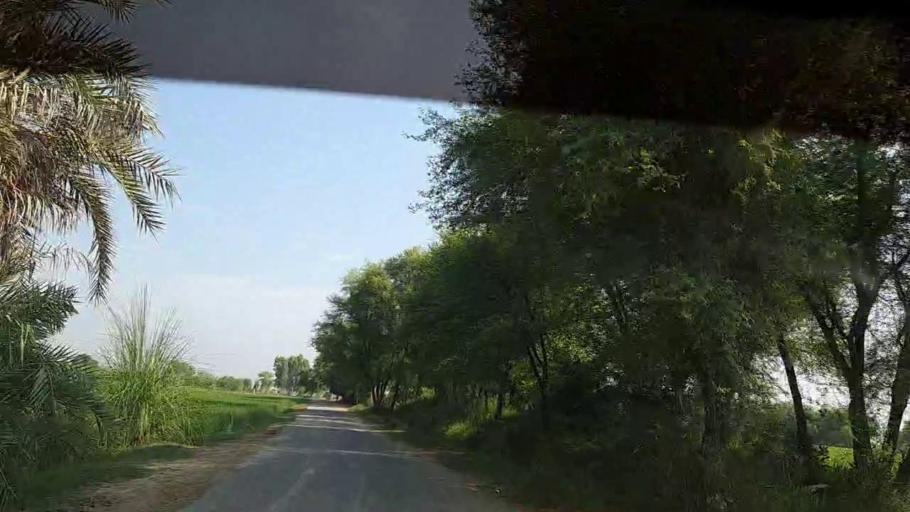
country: PK
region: Sindh
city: Shikarpur
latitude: 28.0928
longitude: 68.6767
